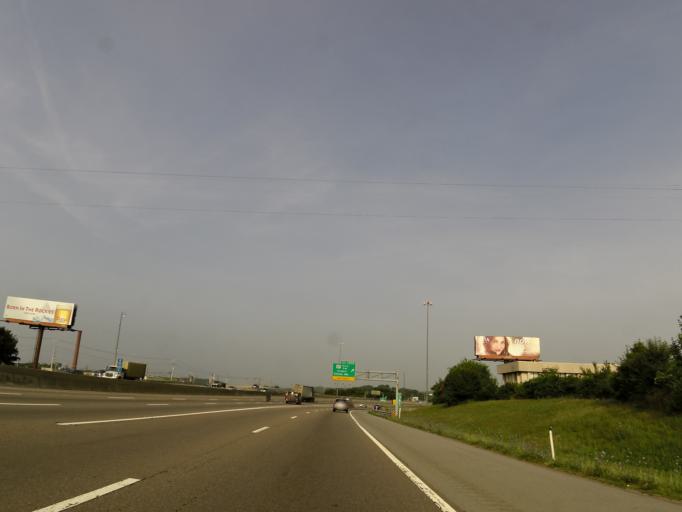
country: US
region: Tennessee
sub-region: Knox County
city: Knoxville
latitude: 35.9634
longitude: -83.9391
